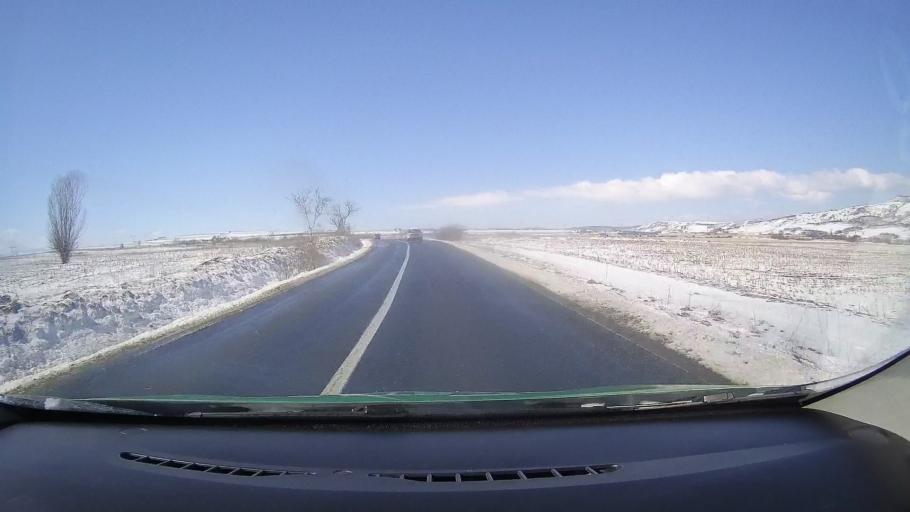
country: RO
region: Sibiu
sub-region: Comuna Rosia
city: Rosia
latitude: 45.7913
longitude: 24.3032
